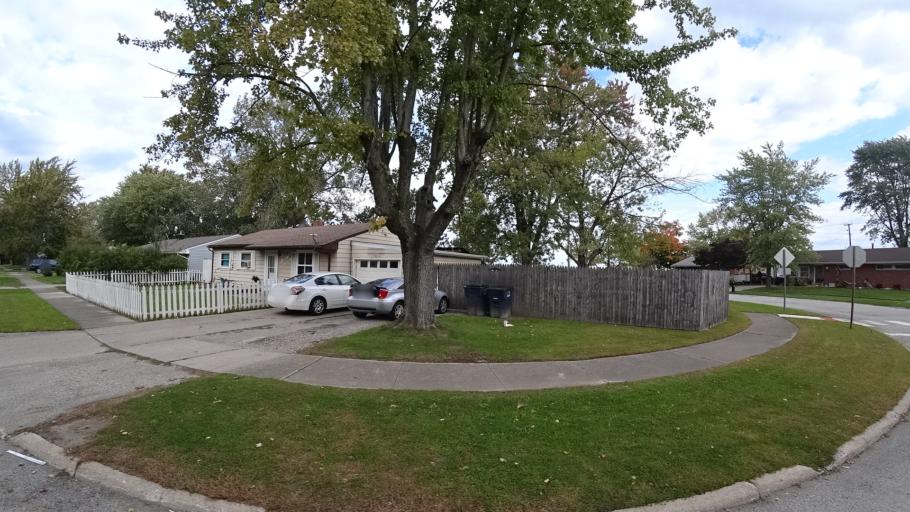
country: US
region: Indiana
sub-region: LaPorte County
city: Michigan City
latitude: 41.6731
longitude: -86.8997
